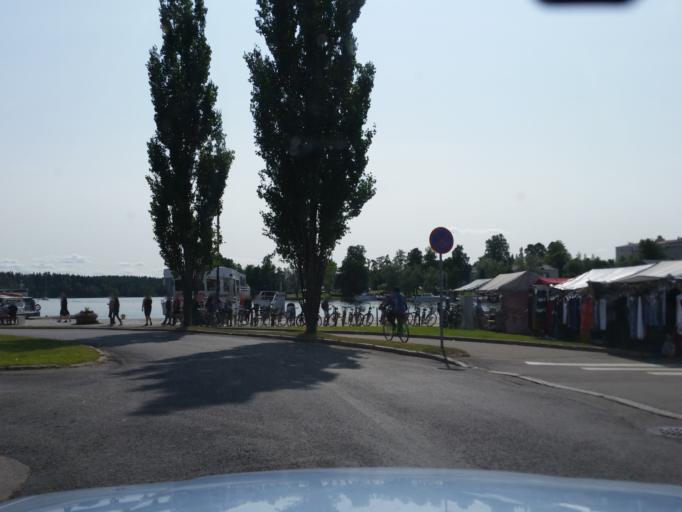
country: FI
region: Southern Savonia
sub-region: Savonlinna
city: Savonlinna
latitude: 61.8676
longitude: 28.8851
